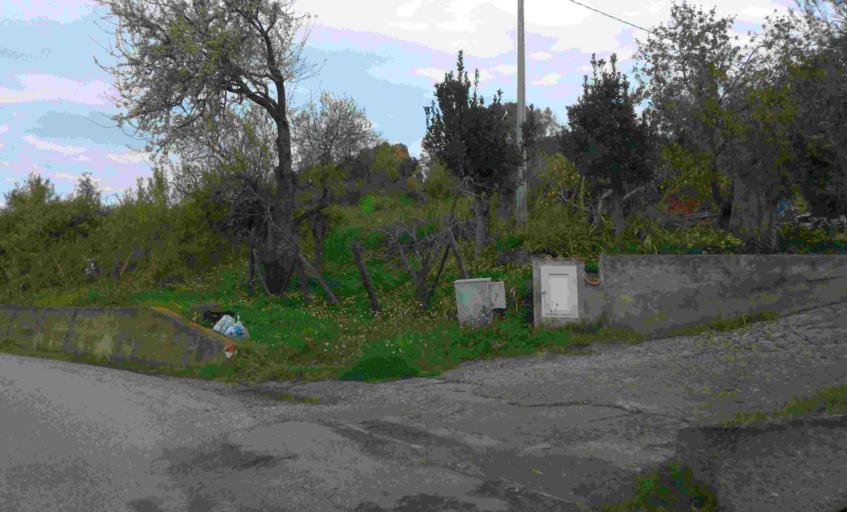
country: IT
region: Calabria
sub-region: Provincia di Catanzaro
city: Sellia Marina
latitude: 38.8888
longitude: 16.7089
